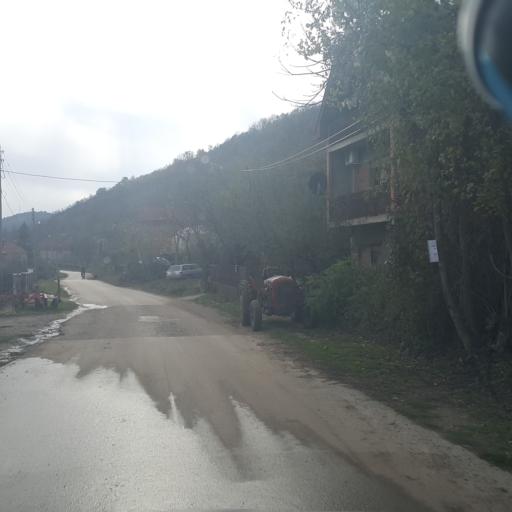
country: RS
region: Central Serbia
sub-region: Zajecarski Okrug
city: Knjazevac
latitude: 43.5958
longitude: 22.2547
